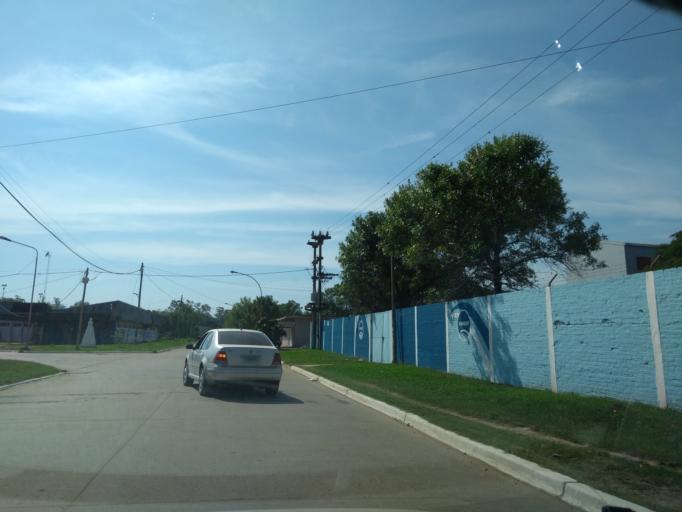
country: AR
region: Chaco
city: Barranqueras
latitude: -27.4642
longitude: -58.9490
